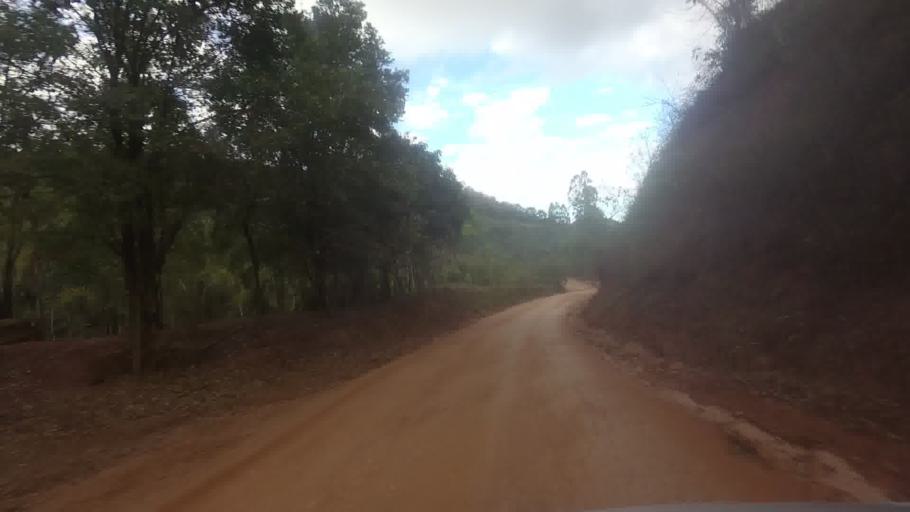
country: BR
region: Espirito Santo
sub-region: Mimoso Do Sul
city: Mimoso do Sul
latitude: -20.9452
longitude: -41.4053
